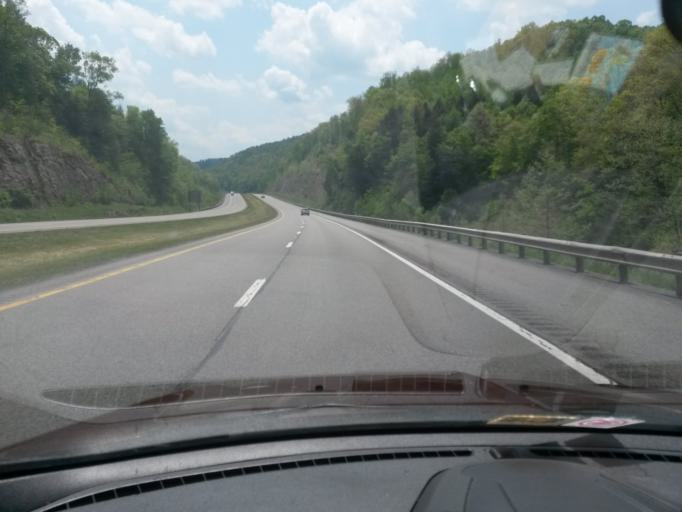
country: US
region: West Virginia
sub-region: Braxton County
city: Sutton
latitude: 38.5918
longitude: -80.7352
